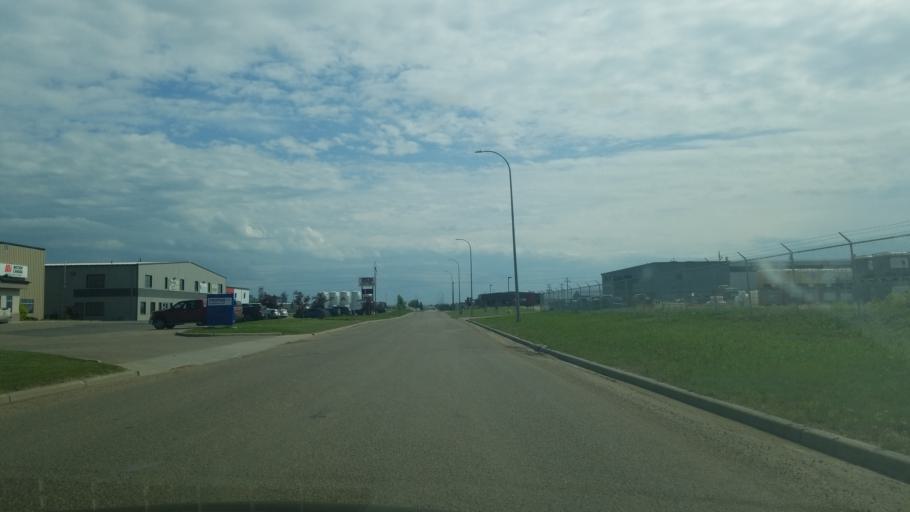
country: CA
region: Saskatchewan
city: Lloydminster
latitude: 53.2950
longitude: -110.0367
